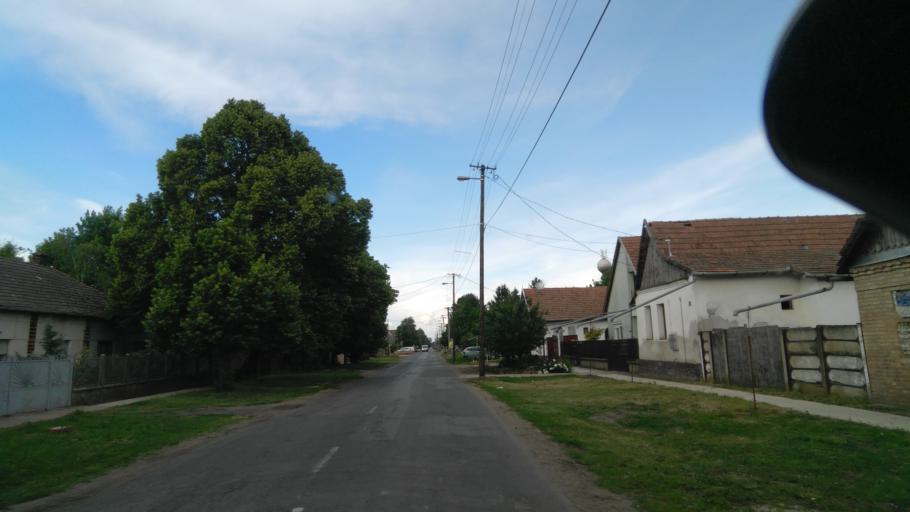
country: HU
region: Bekes
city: Kevermes
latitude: 46.4141
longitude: 21.1778
